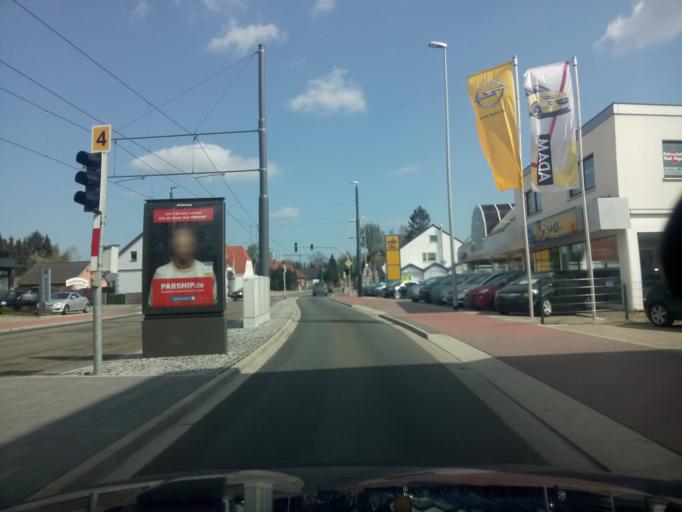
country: DE
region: Lower Saxony
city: Lilienthal
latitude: 53.1541
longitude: 8.9282
